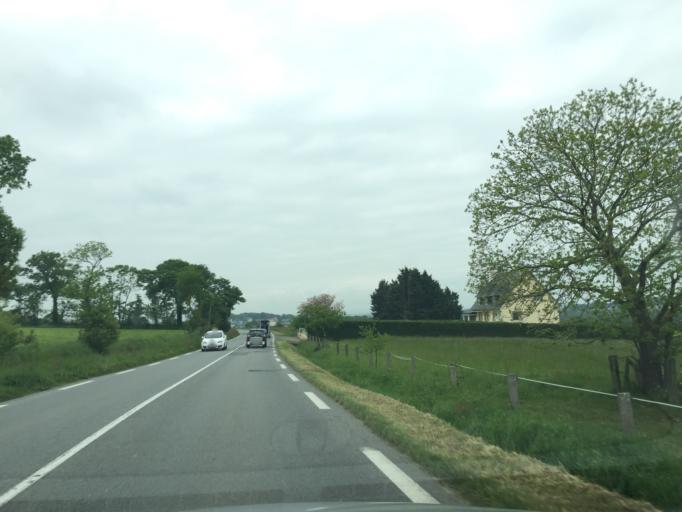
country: FR
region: Brittany
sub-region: Departement des Cotes-d'Armor
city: Lamballe
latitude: 48.4865
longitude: -2.4867
